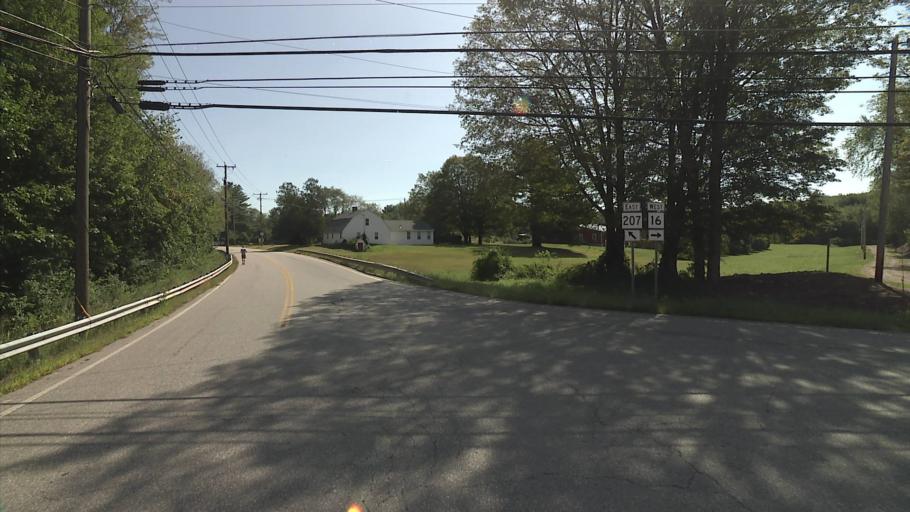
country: US
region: Connecticut
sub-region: New London County
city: Colchester
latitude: 41.6174
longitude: -72.2716
